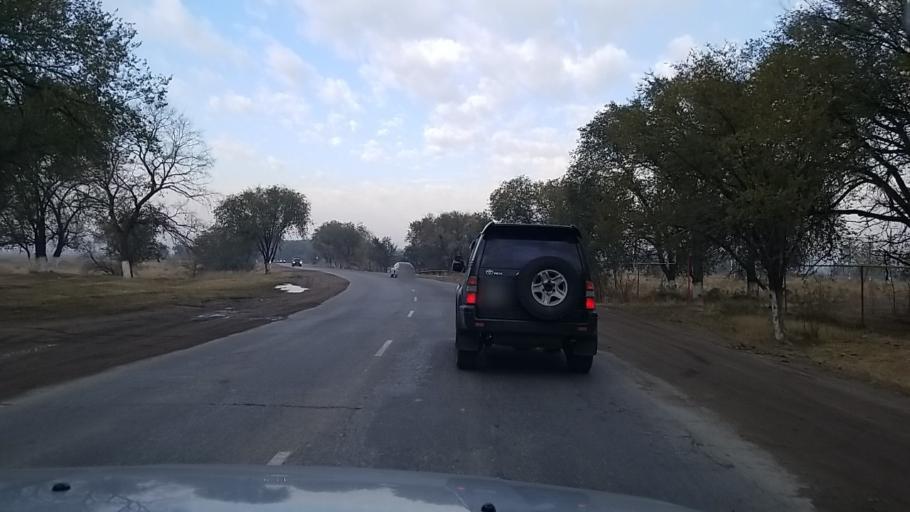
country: KZ
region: Almaty Oblysy
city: Burunday
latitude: 43.3605
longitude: 76.7488
